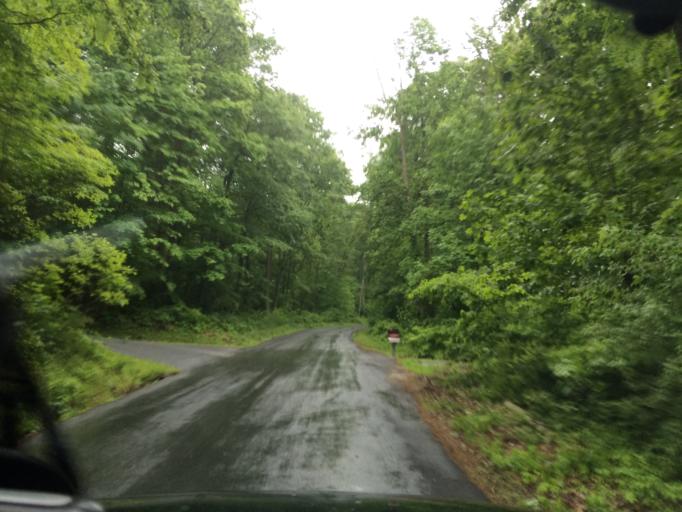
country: US
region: Maryland
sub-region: Washington County
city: Highfield-Cascade
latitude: 39.7049
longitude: -77.4675
